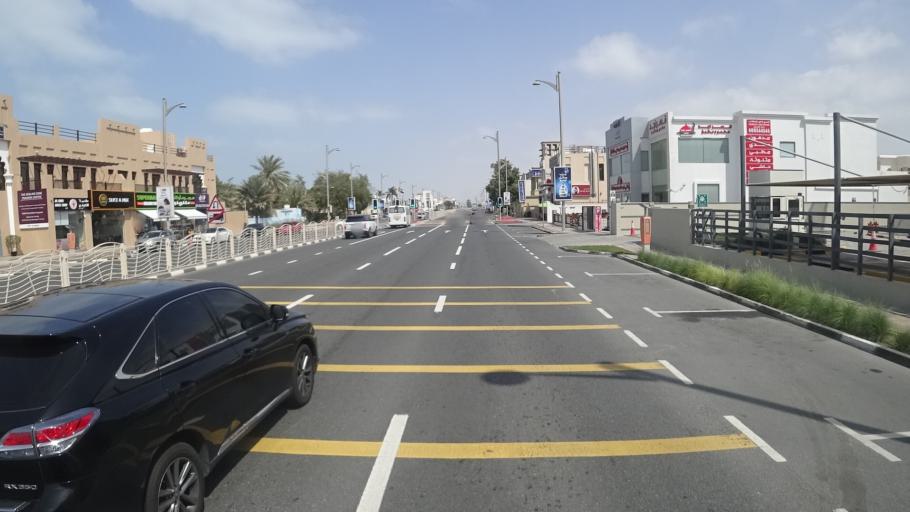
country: AE
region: Dubai
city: Dubai
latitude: 25.1668
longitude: 55.2141
